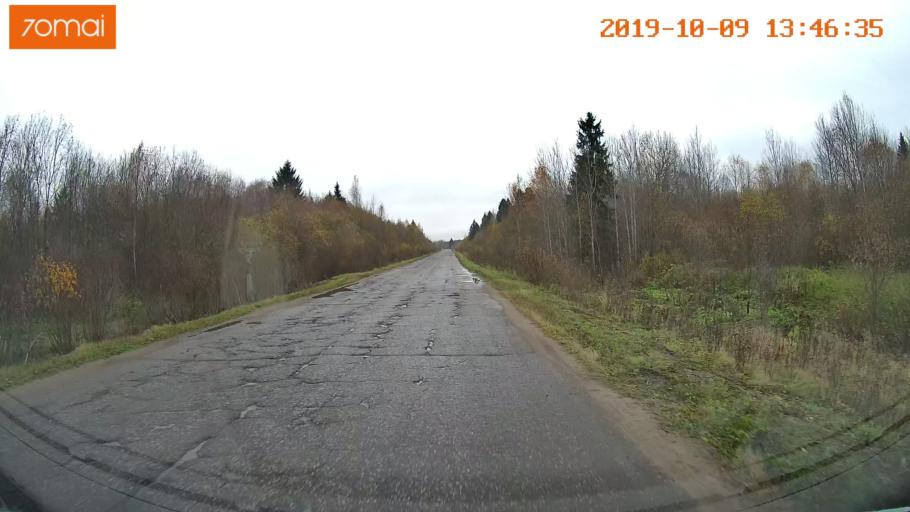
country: RU
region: Kostroma
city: Buy
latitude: 58.3847
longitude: 41.2189
